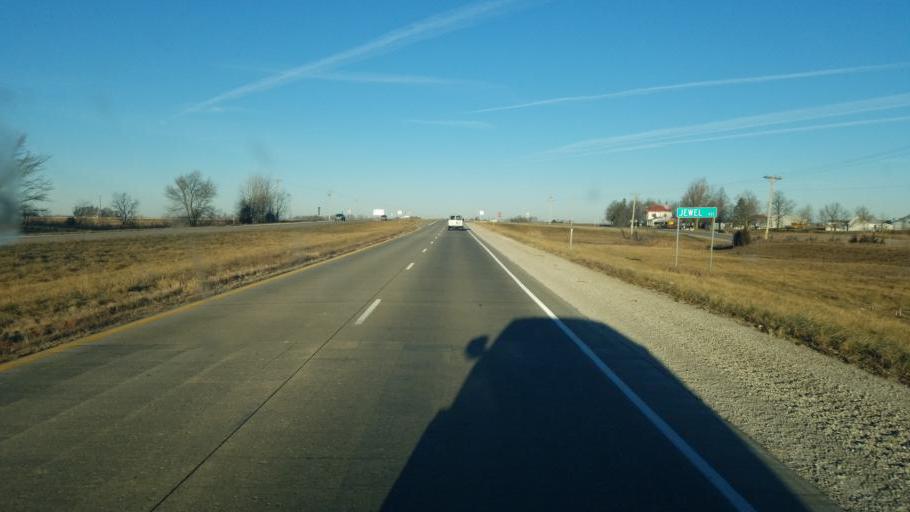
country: US
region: Iowa
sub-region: Mahaska County
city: Oskaloosa
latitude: 41.3132
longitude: -92.6860
